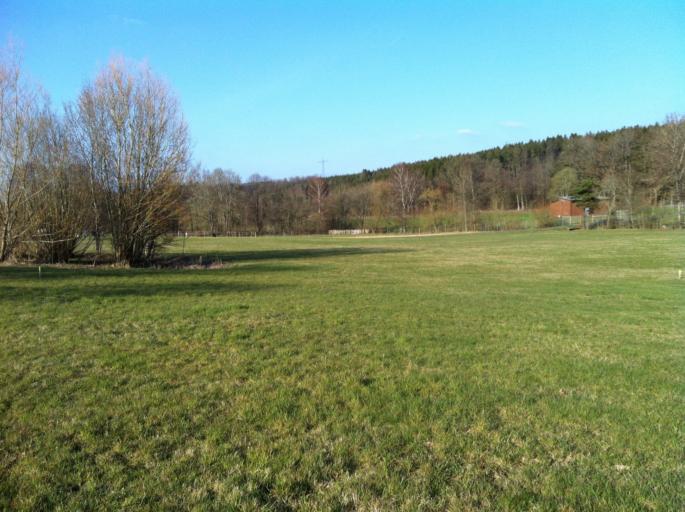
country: DE
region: Baden-Wuerttemberg
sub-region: Karlsruhe Region
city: Mudau
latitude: 49.5386
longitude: 9.2088
